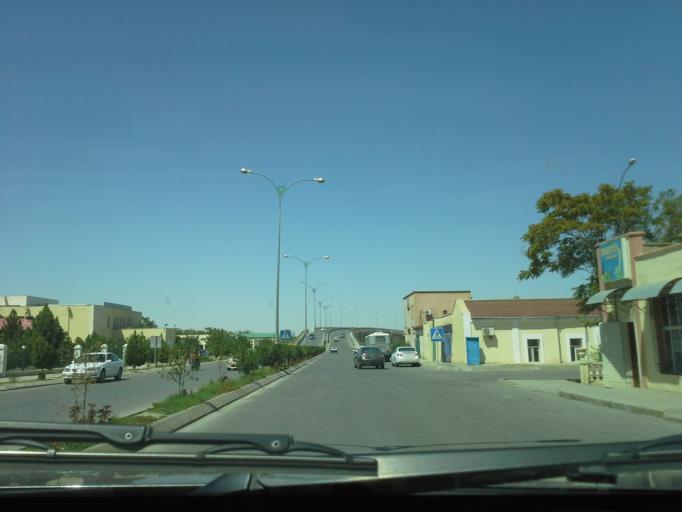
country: TM
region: Balkan
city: Serdar
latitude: 38.9756
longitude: 56.2778
